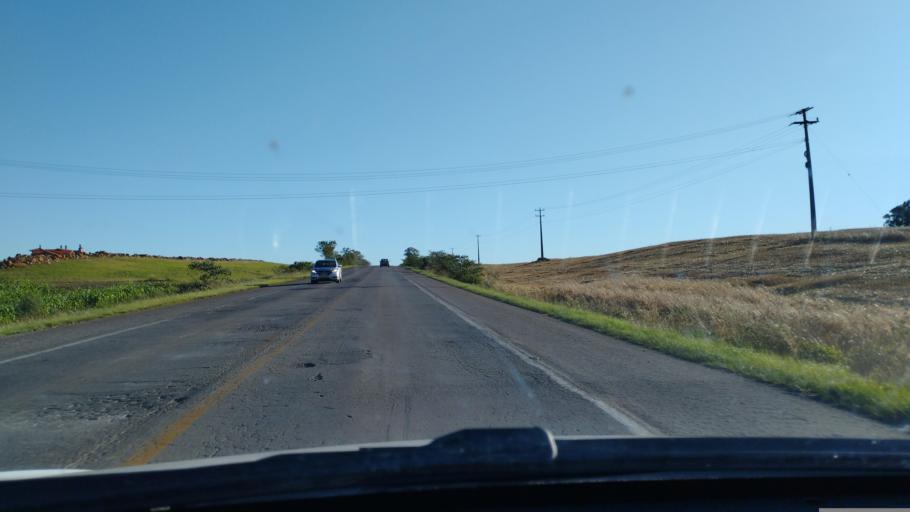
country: BR
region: Rio Grande do Sul
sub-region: Julio De Castilhos
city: Julio de Castilhos
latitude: -29.4235
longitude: -53.6730
